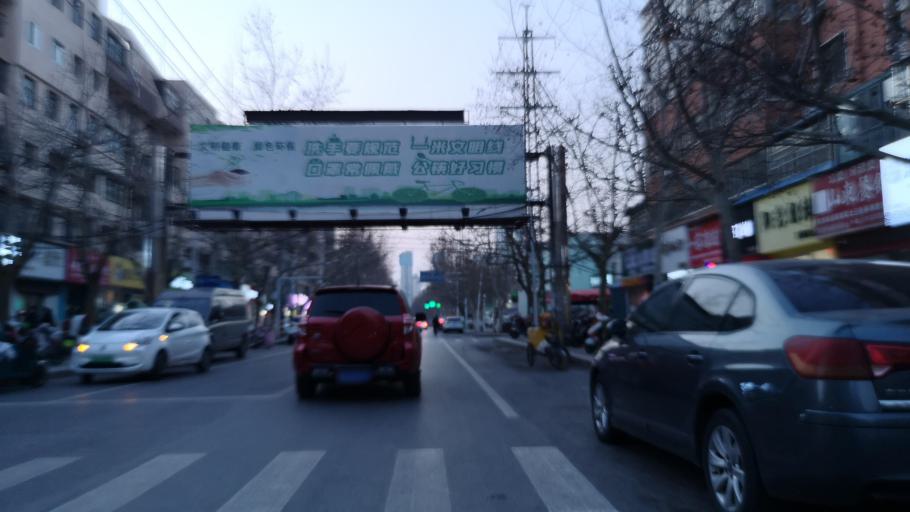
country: CN
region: Henan Sheng
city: Zhongyuanlu
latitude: 35.7662
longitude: 115.0648
